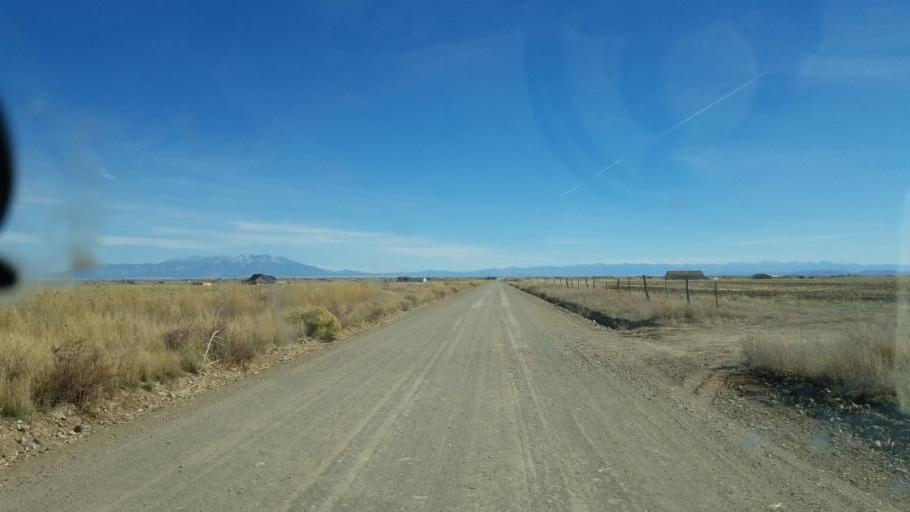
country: US
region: Colorado
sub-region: Rio Grande County
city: Monte Vista
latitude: 37.4011
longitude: -106.1263
